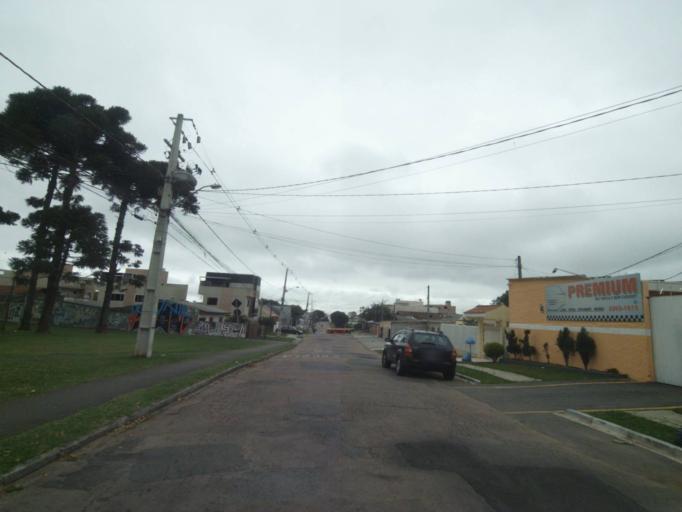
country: BR
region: Parana
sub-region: Sao Jose Dos Pinhais
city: Sao Jose dos Pinhais
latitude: -25.5432
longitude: -49.2841
